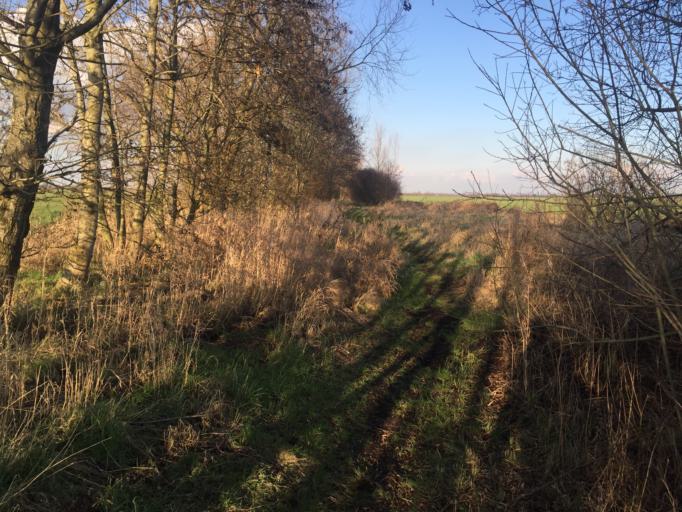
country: NL
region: Utrecht
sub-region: Gemeente Oudewater
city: Oudewater
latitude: 52.0408
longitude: 4.8212
